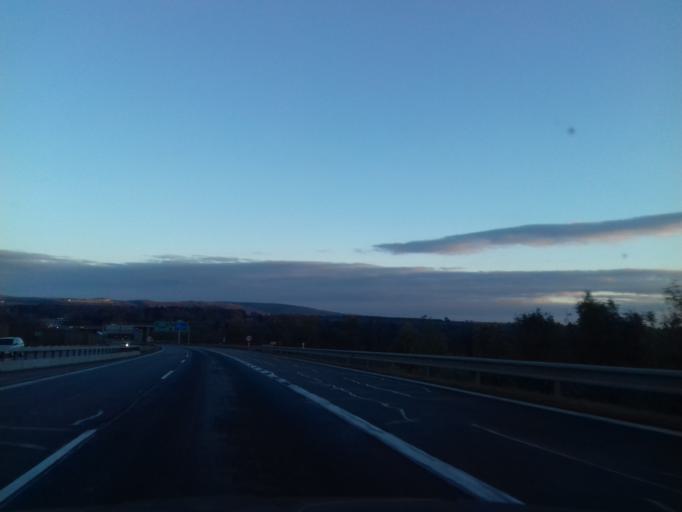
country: CZ
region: South Moravian
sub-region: Okres Vyskov
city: Vyskov
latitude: 49.2752
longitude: 17.0212
